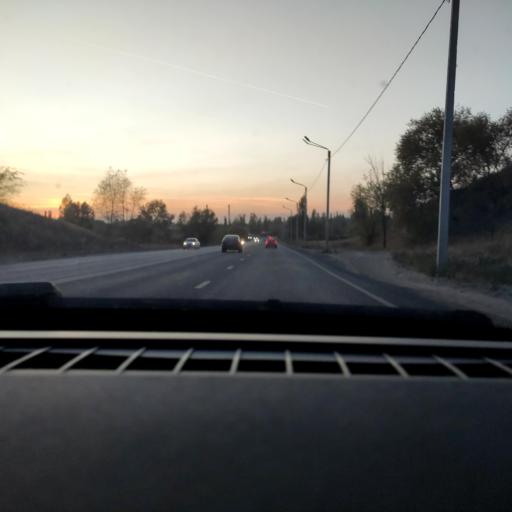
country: RU
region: Voronezj
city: Maslovka
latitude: 51.6215
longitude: 39.2670
